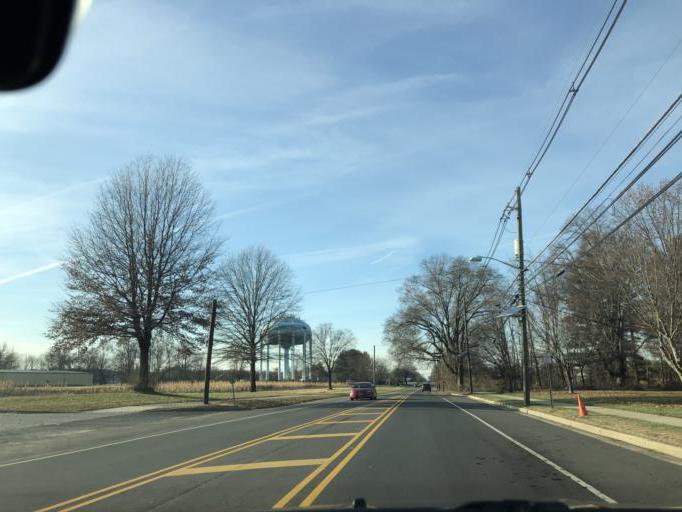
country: US
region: New Jersey
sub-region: Burlington County
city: Moorestown-Lenola
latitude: 39.9710
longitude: -74.9699
